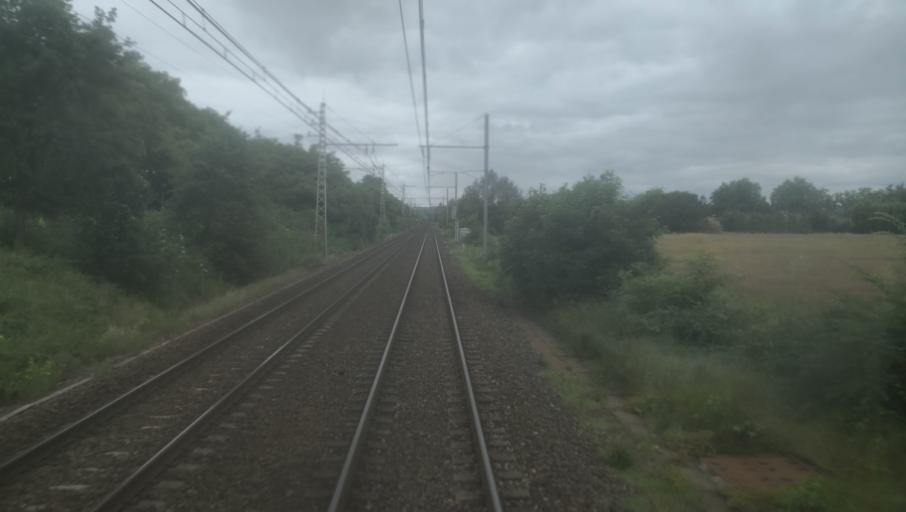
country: FR
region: Midi-Pyrenees
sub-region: Departement de la Haute-Garonne
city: Saint-Jory
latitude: 43.7491
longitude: 1.3637
